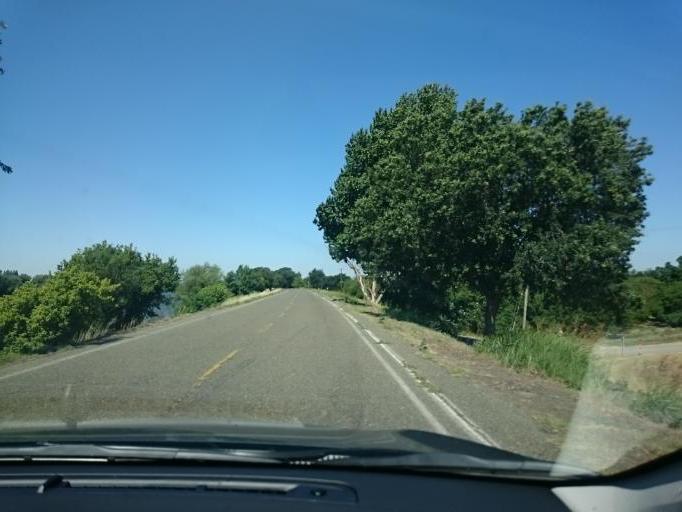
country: US
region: California
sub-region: Yolo County
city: West Sacramento
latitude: 38.5179
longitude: -121.5367
